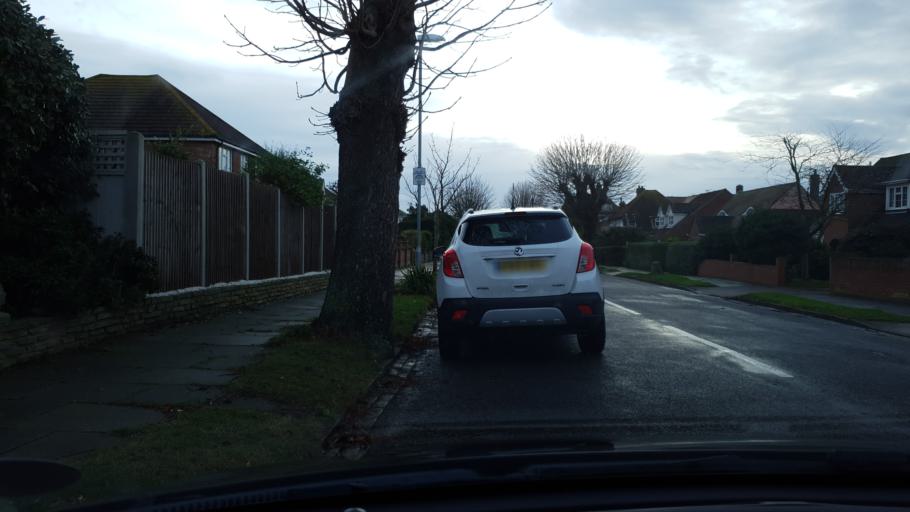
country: GB
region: England
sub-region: Essex
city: Frinton-on-Sea
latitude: 51.8347
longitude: 1.2511
